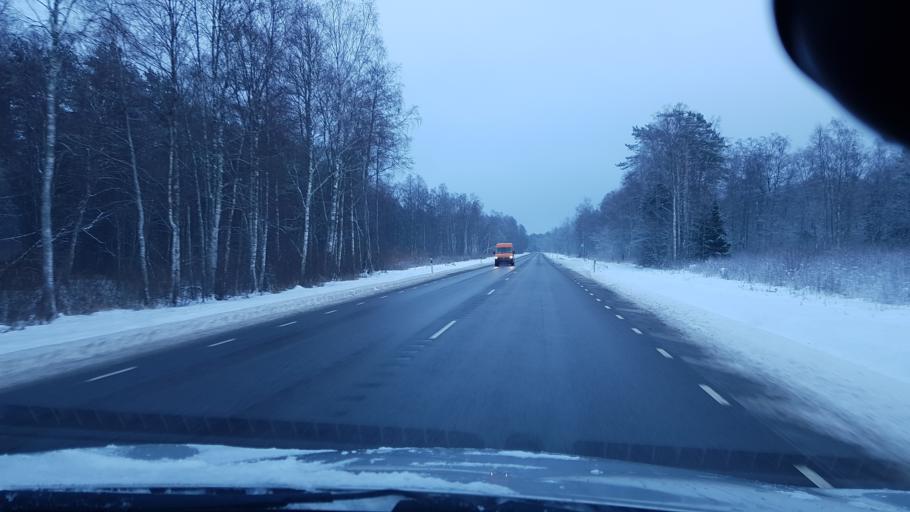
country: EE
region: Harju
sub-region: Paldiski linn
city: Paldiski
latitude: 59.3377
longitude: 24.2259
